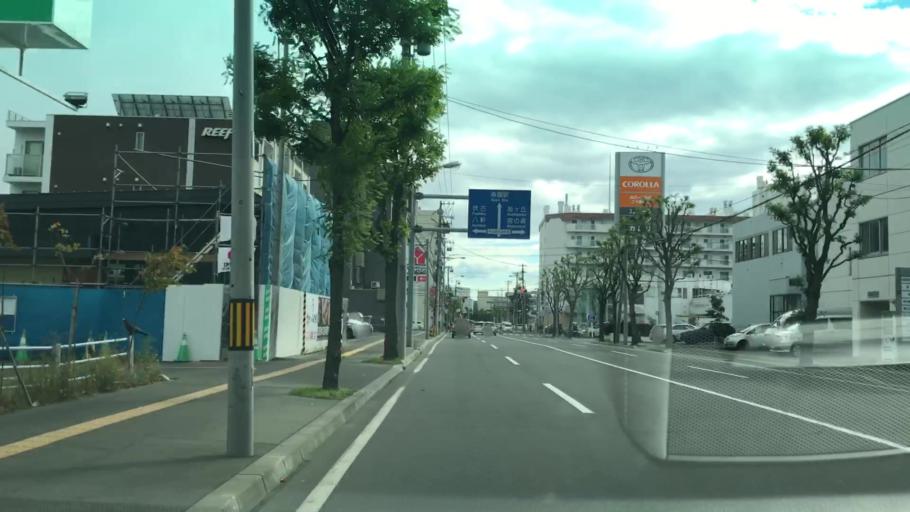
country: JP
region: Hokkaido
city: Sapporo
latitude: 43.0761
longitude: 141.3130
